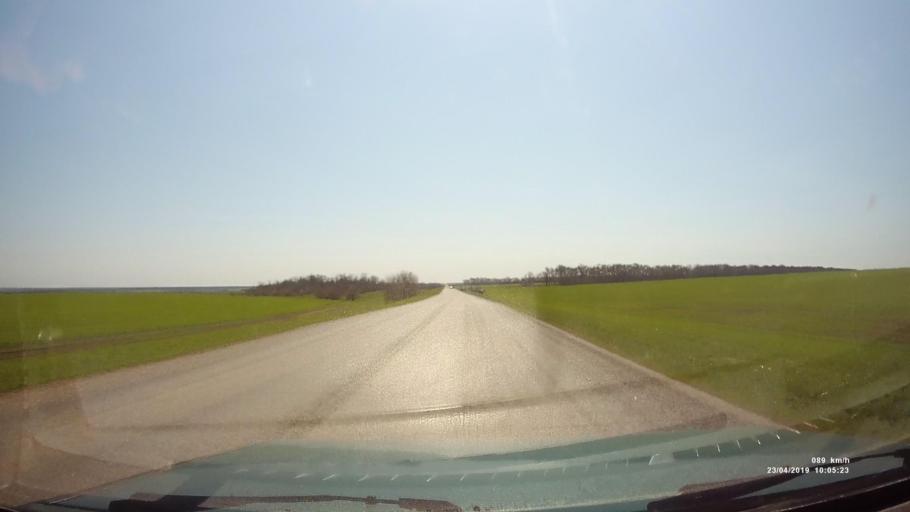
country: RU
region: Rostov
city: Sovetskoye
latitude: 46.7415
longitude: 42.2190
